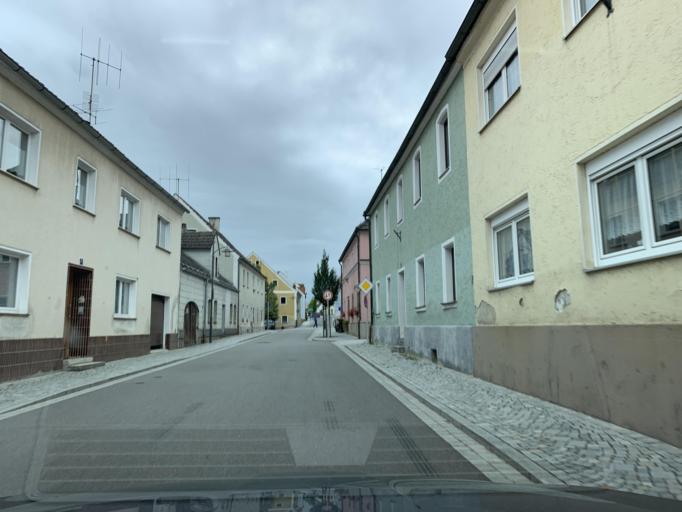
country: DE
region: Bavaria
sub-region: Upper Palatinate
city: Schwarzhofen
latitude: 49.3772
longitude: 12.3446
